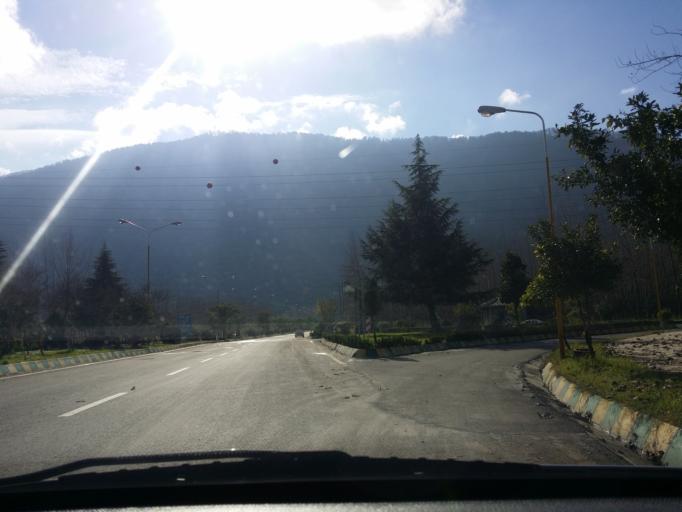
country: IR
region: Mazandaran
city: Chalus
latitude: 36.6762
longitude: 51.3067
